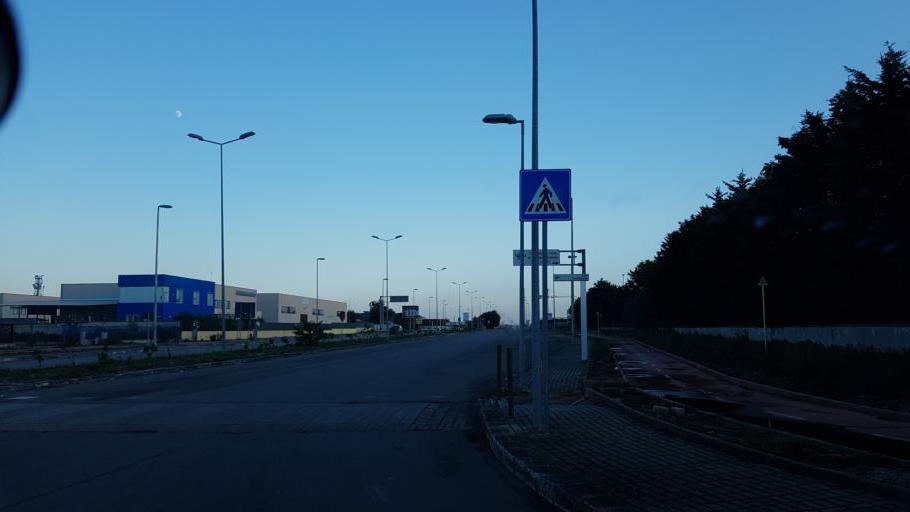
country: IT
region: Apulia
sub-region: Provincia di Lecce
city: Surbo
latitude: 40.3799
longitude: 18.1254
